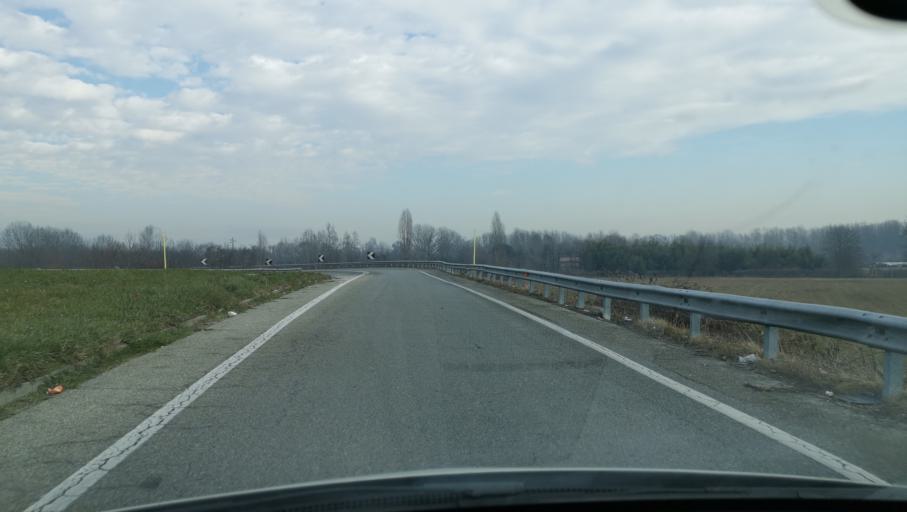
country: IT
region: Piedmont
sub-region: Provincia di Torino
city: Brandizzo
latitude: 45.1855
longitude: 7.8598
